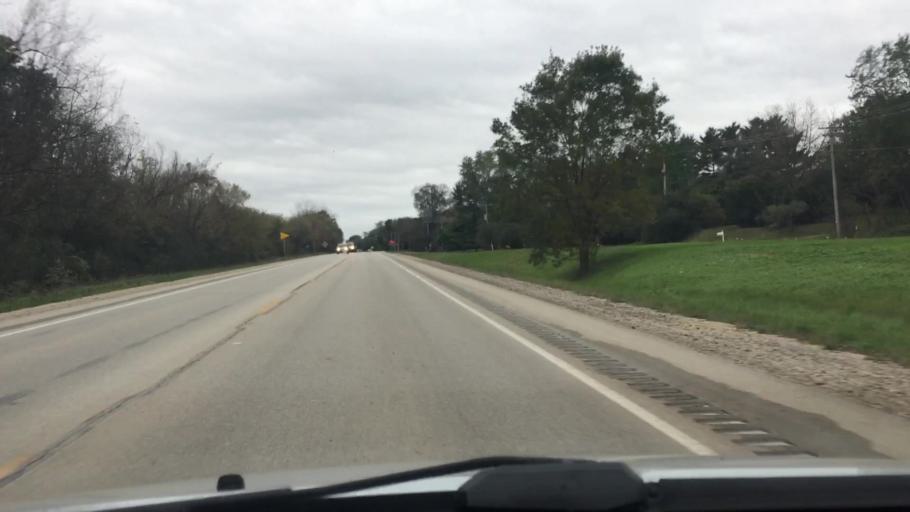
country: US
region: Wisconsin
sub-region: Waukesha County
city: Waukesha
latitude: 42.9780
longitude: -88.2827
